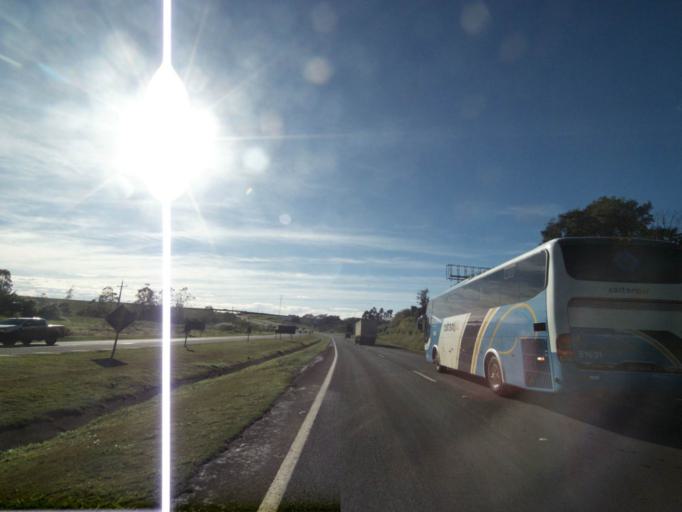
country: BR
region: Parana
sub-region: Cascavel
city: Cascavel
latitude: -25.0279
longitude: -53.5571
